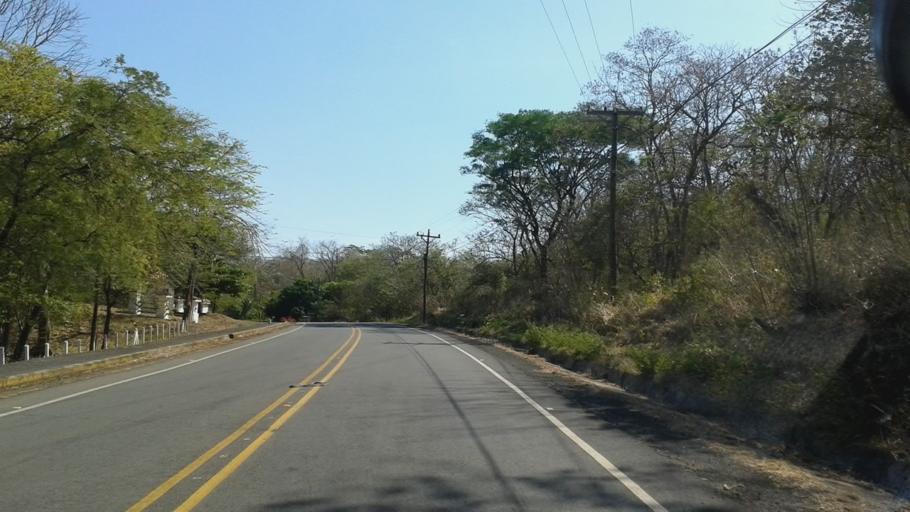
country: CR
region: Guanacaste
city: Santa Cruz
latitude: 10.2044
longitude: -85.7619
